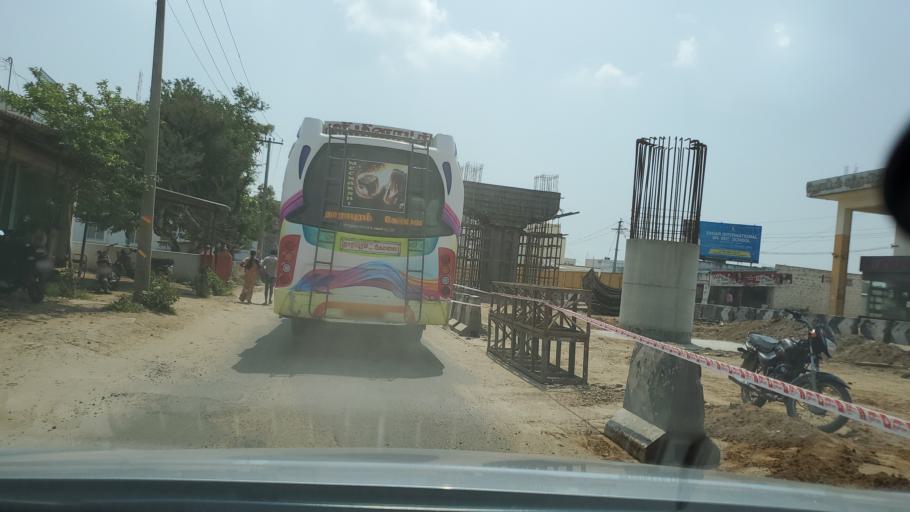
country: IN
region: Tamil Nadu
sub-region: Tiruppur
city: Dharapuram
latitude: 10.7365
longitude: 77.5173
